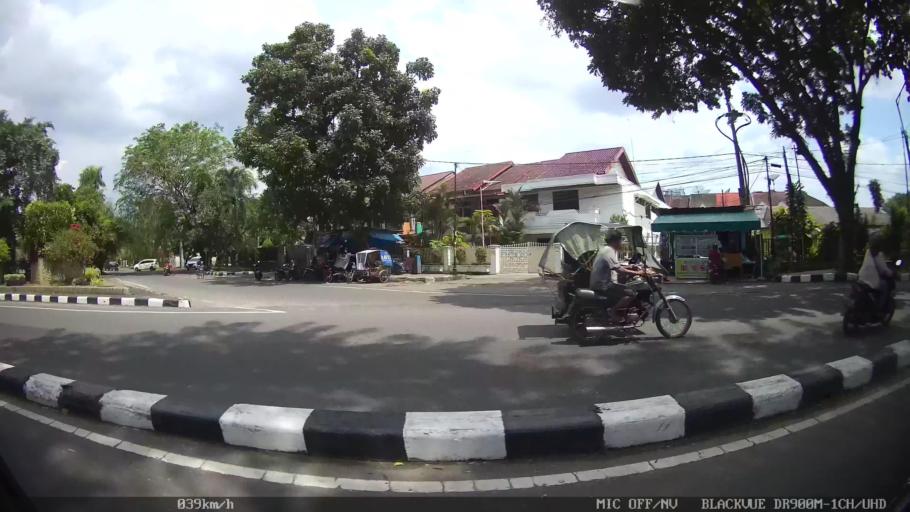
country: ID
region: North Sumatra
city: Medan
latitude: 3.5708
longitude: 98.6714
